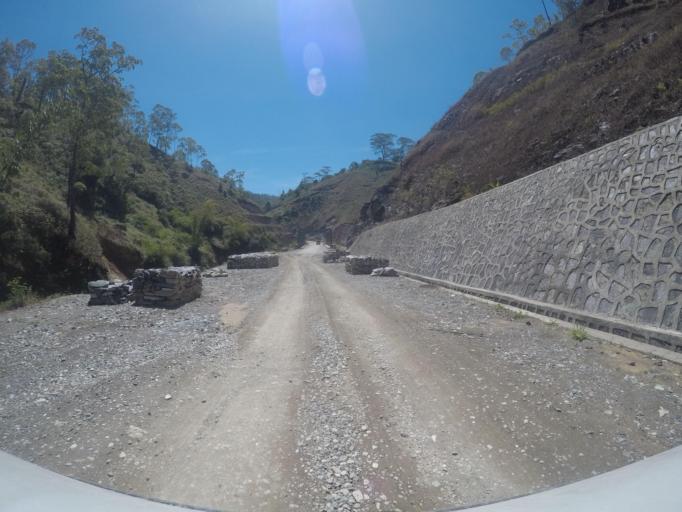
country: TL
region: Ermera
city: Gleno
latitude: -8.7789
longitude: 125.3822
